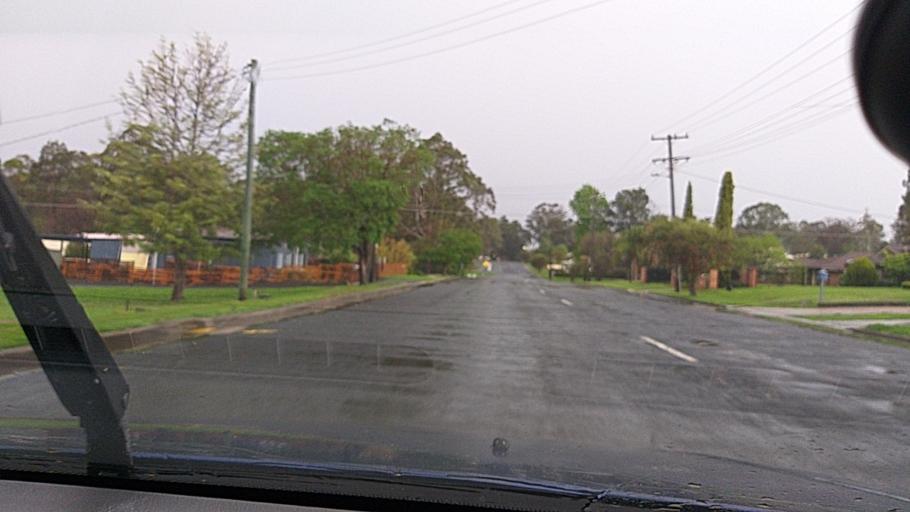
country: AU
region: New South Wales
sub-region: Wollondilly
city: Douglas Park
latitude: -34.1850
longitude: 150.7111
